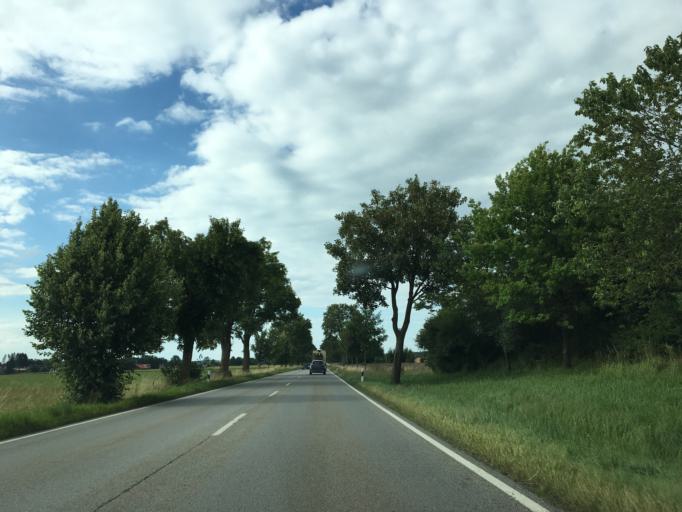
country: DE
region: Bavaria
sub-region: Upper Bavaria
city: Holzkirchen
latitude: 47.8647
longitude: 11.7188
